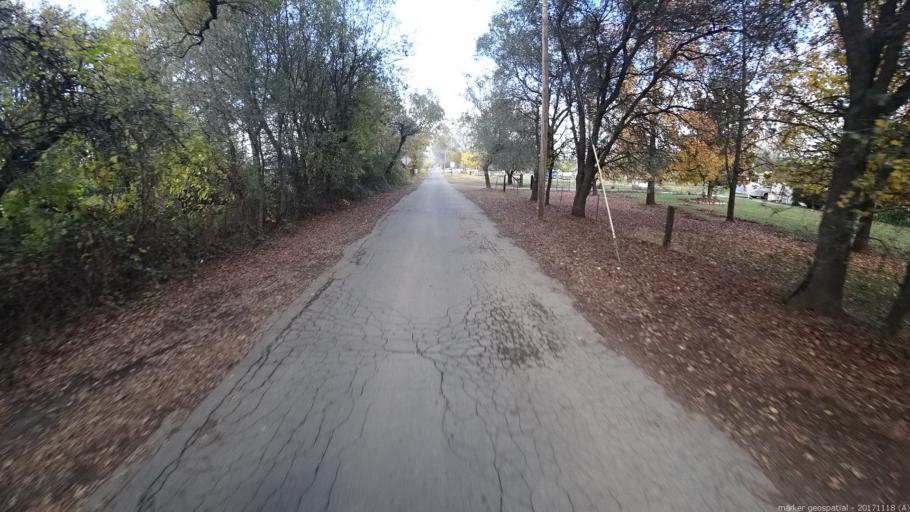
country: US
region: California
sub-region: Shasta County
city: Anderson
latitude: 40.4517
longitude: -122.3244
